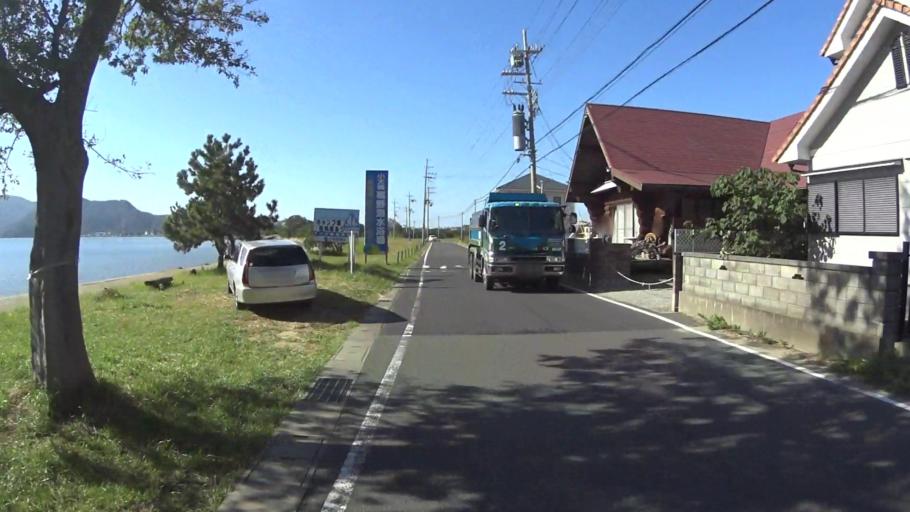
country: JP
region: Hyogo
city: Toyooka
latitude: 35.6405
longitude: 134.9231
